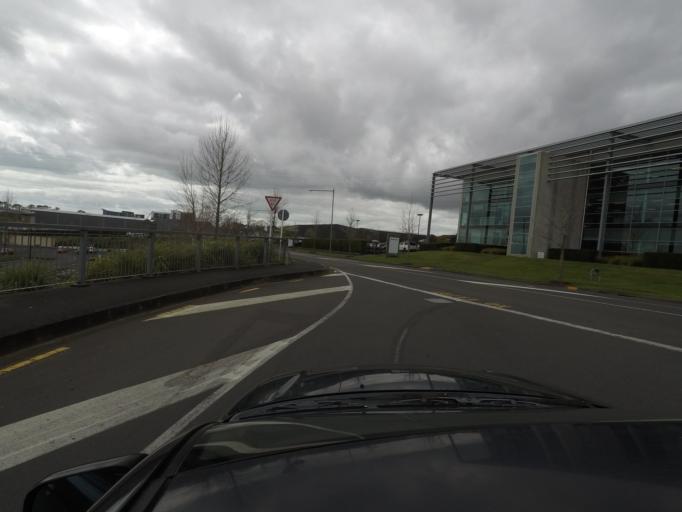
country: NZ
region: Auckland
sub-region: Auckland
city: Tamaki
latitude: -36.9398
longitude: 174.8698
